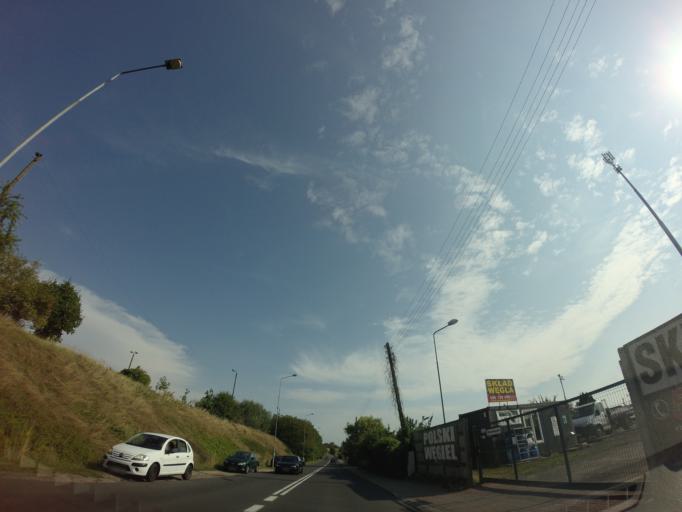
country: PL
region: West Pomeranian Voivodeship
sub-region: Powiat stargardzki
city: Stargard Szczecinski
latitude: 53.3313
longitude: 15.0366
